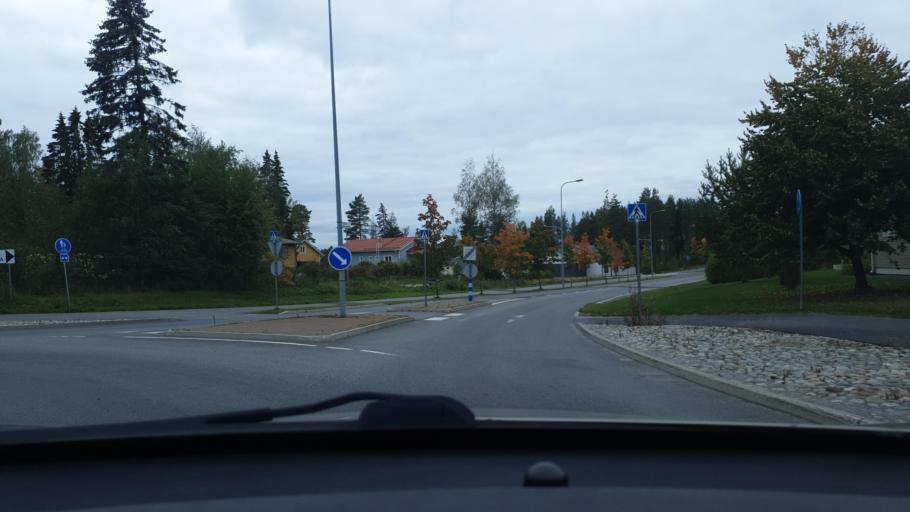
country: FI
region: Ostrobothnia
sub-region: Vaasa
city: Korsholm
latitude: 63.1033
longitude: 21.6784
